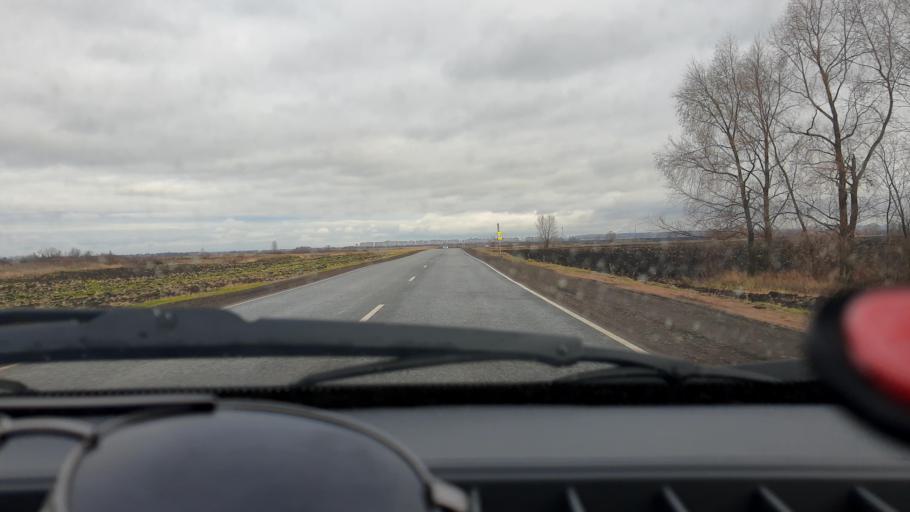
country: RU
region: Bashkortostan
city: Ufa
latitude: 54.8057
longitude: 55.9644
